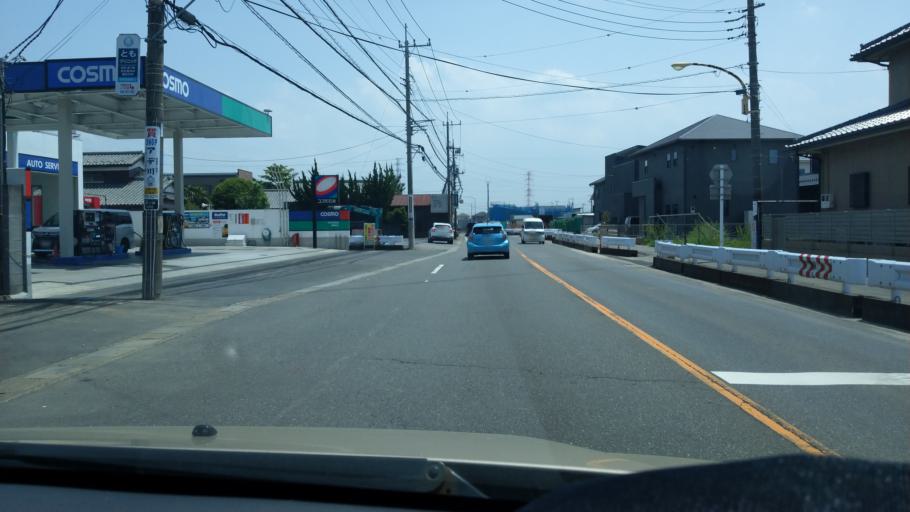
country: JP
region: Saitama
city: Koshigaya
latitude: 35.9060
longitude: 139.7306
